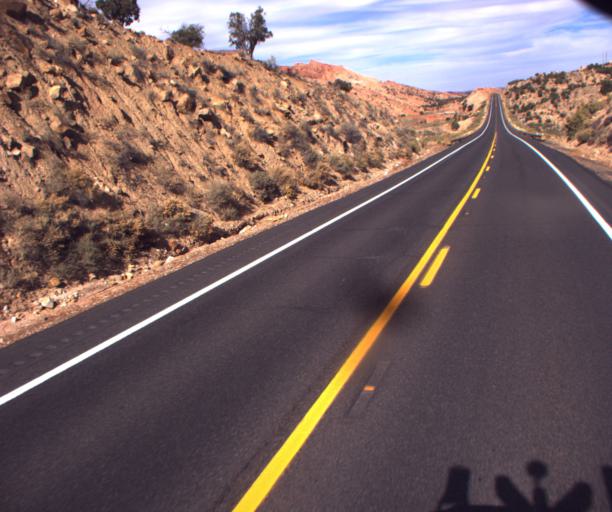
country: US
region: Arizona
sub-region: Navajo County
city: Kayenta
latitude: 36.6534
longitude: -110.4252
